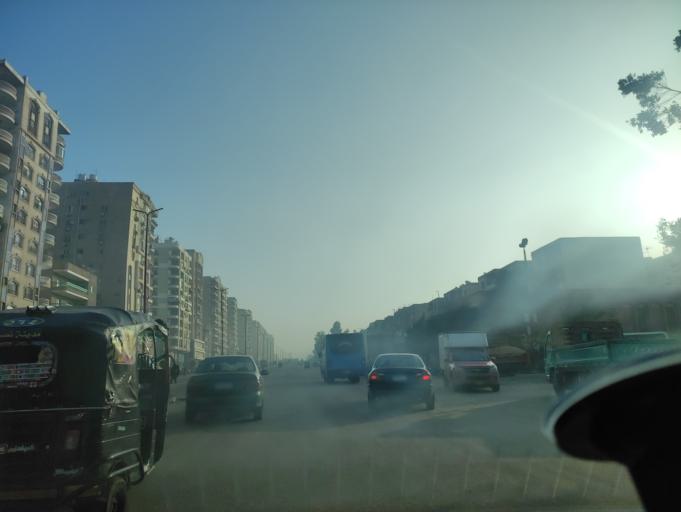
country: EG
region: Muhafazat al Qahirah
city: Cairo
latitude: 30.0480
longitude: 31.3707
